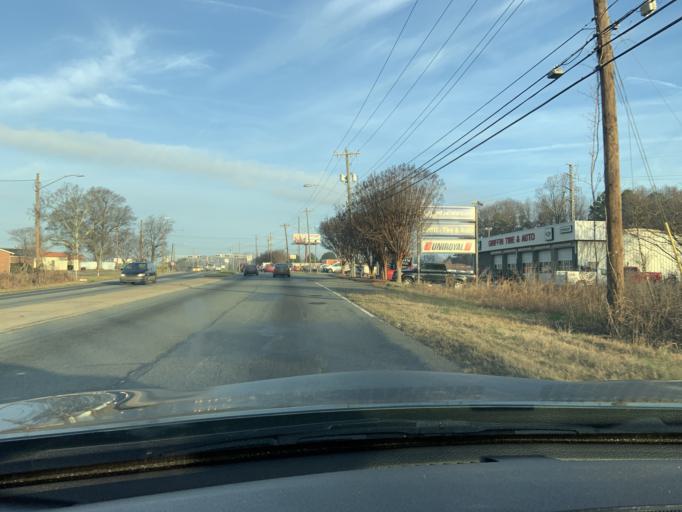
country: US
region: North Carolina
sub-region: Mecklenburg County
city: Charlotte
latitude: 35.2712
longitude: -80.8838
